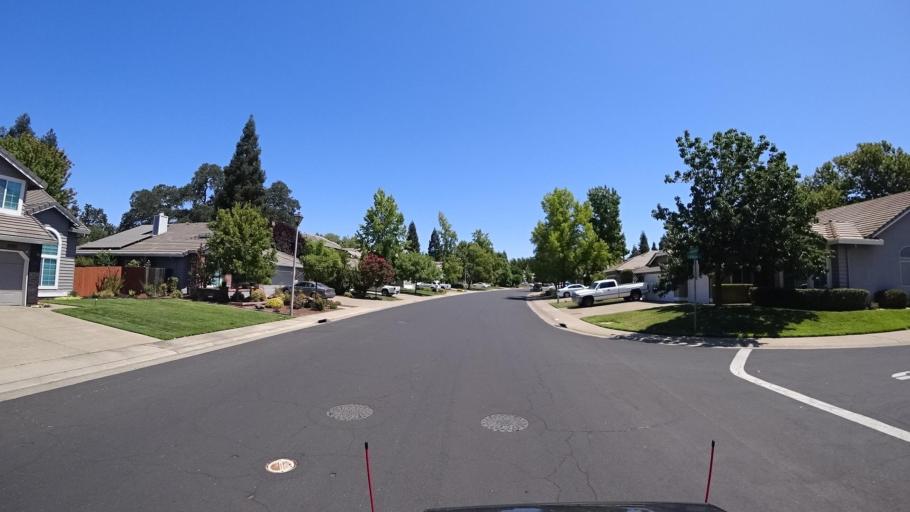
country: US
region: California
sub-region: Placer County
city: Rocklin
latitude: 38.8255
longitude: -121.2547
